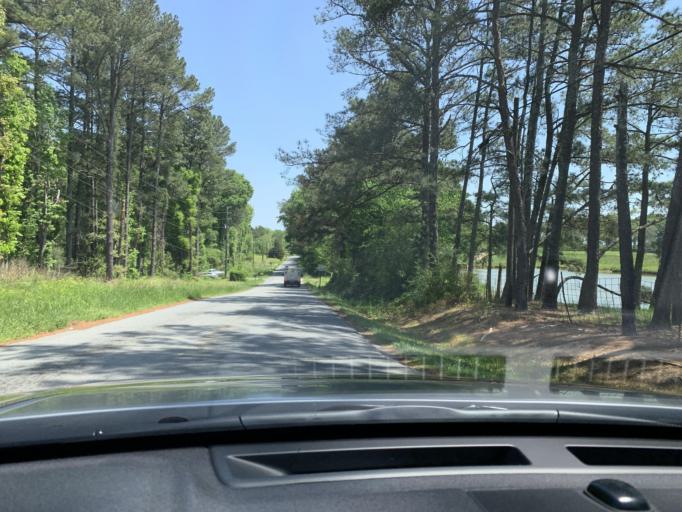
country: US
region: Georgia
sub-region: Polk County
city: Cedartown
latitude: 34.0362
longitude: -85.2020
